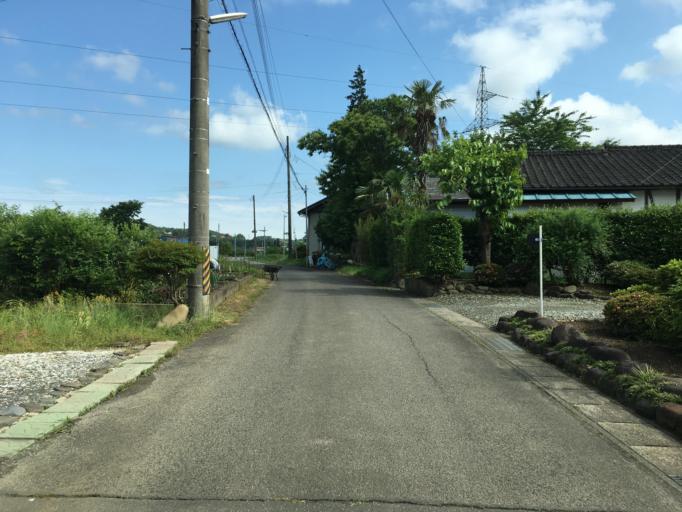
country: JP
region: Fukushima
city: Fukushima-shi
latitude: 37.7340
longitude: 140.4007
